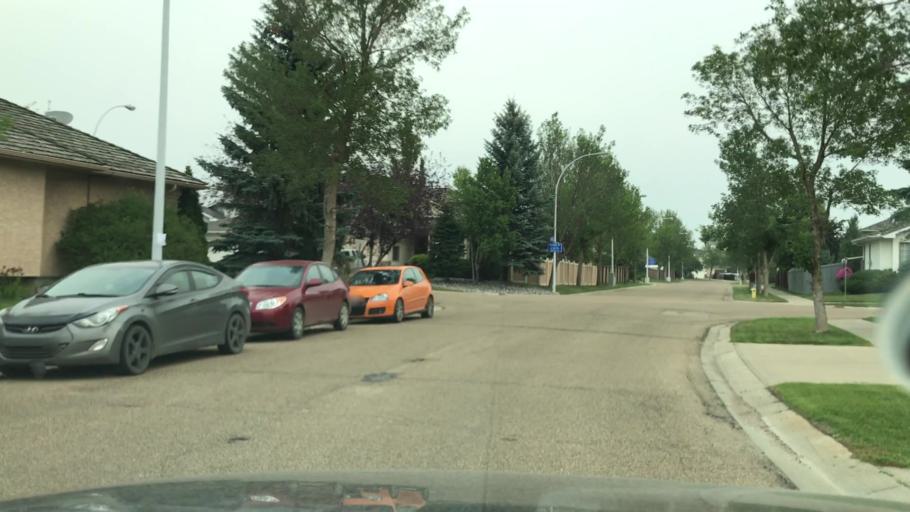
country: CA
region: Alberta
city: Edmonton
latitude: 53.4698
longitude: -113.5774
